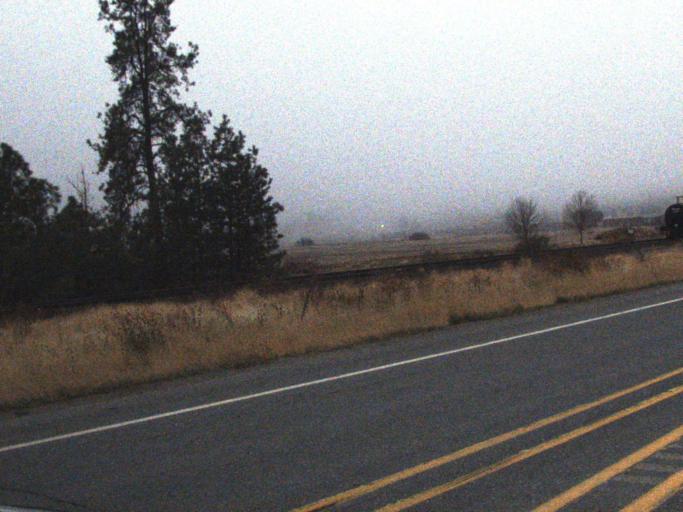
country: US
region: Washington
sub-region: Stevens County
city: Kettle Falls
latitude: 48.6099
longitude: -118.0357
